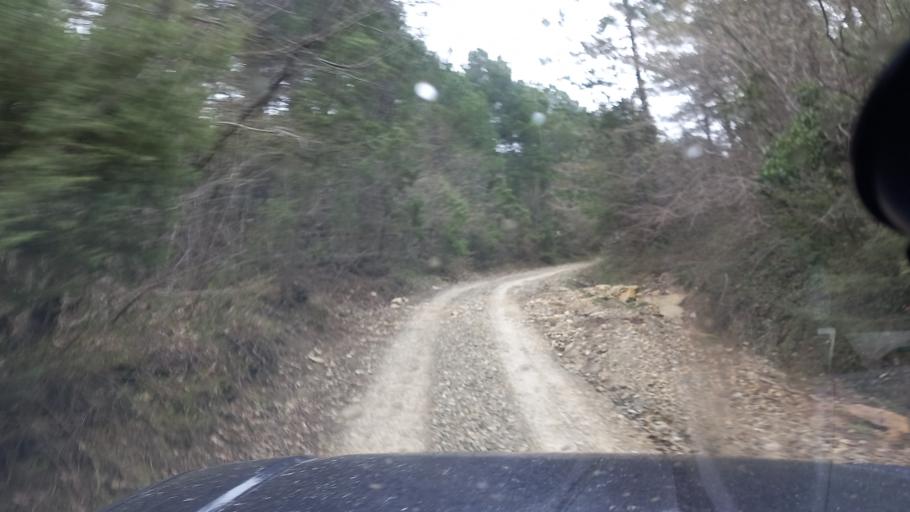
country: RU
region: Krasnodarskiy
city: Arkhipo-Osipovka
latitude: 44.3760
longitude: 38.4612
